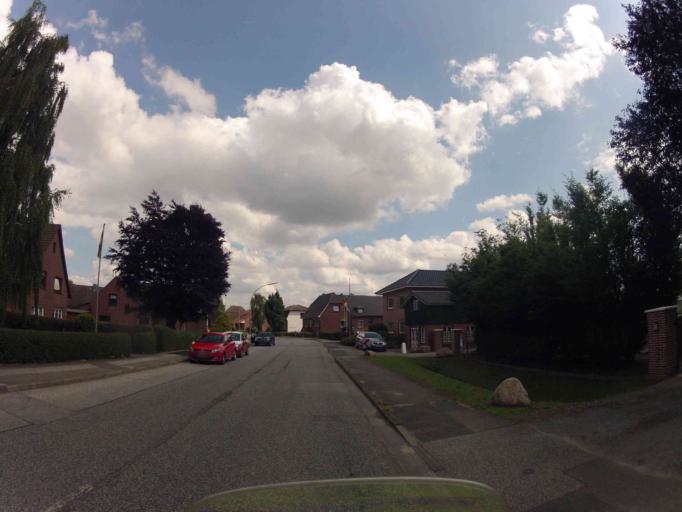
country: DE
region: Lower Saxony
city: Stelle
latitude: 53.4209
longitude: 10.1457
